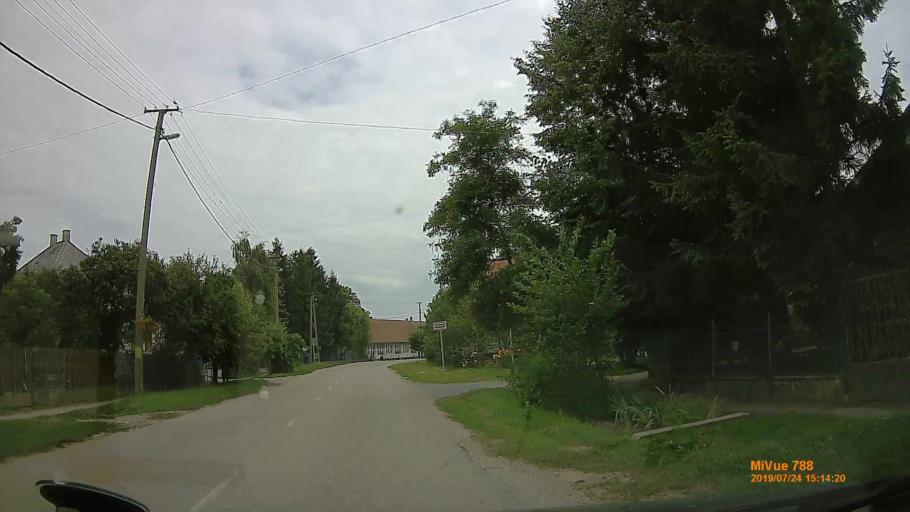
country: HU
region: Szabolcs-Szatmar-Bereg
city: Tarpa
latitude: 48.2001
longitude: 22.5242
